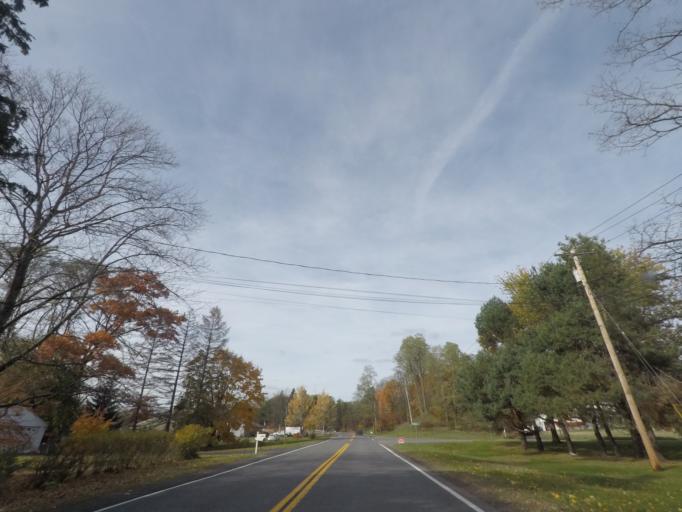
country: US
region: New York
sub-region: Albany County
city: Westmere
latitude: 42.7246
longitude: -73.8855
